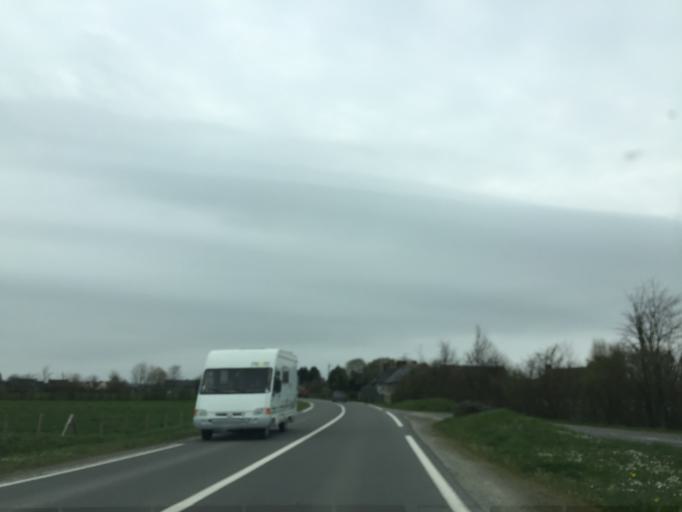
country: FR
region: Brittany
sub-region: Departement d'Ille-et-Vilaine
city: Cherrueix
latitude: 48.6041
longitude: -1.7187
